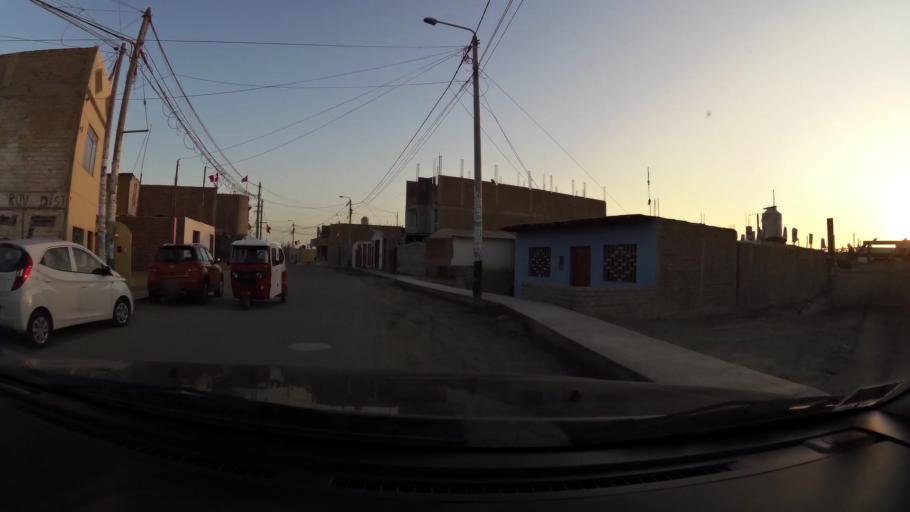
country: PE
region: Ica
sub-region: Provincia de Pisco
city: San Clemente
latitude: -13.6746
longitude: -76.1595
